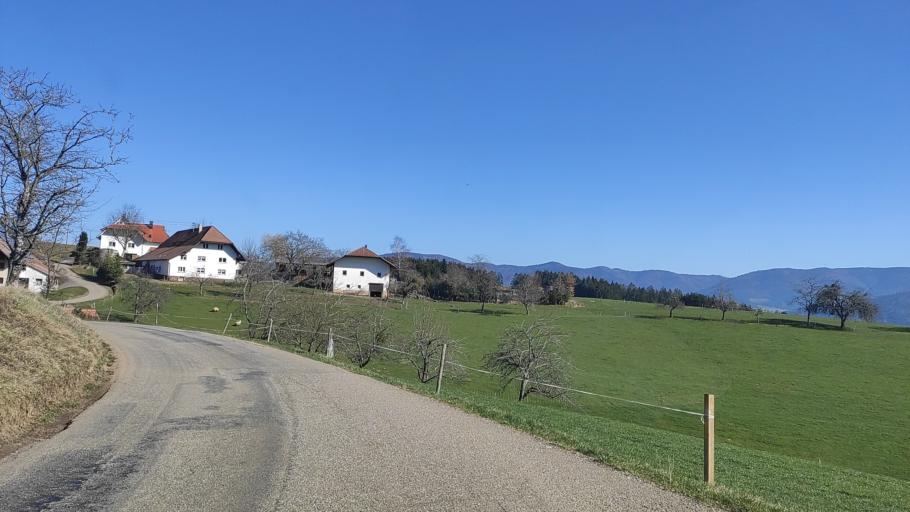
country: DE
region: Baden-Wuerttemberg
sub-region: Freiburg Region
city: Elzach
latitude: 48.1806
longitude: 8.0212
